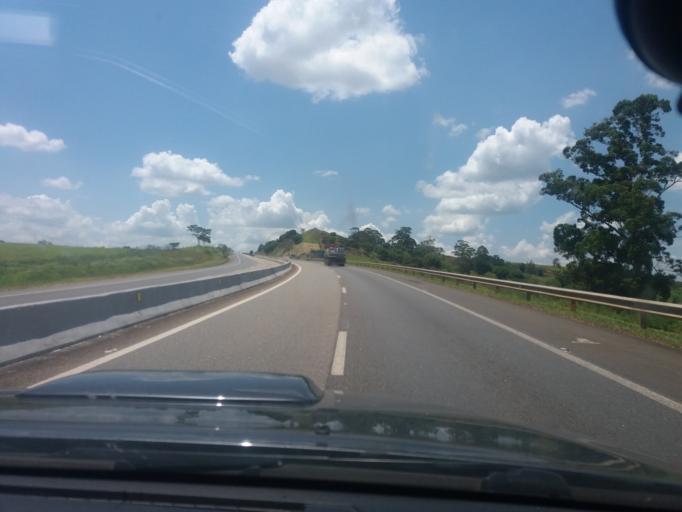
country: BR
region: Sao Paulo
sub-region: Itapetininga
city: Itapetininga
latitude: -23.4852
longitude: -47.9744
